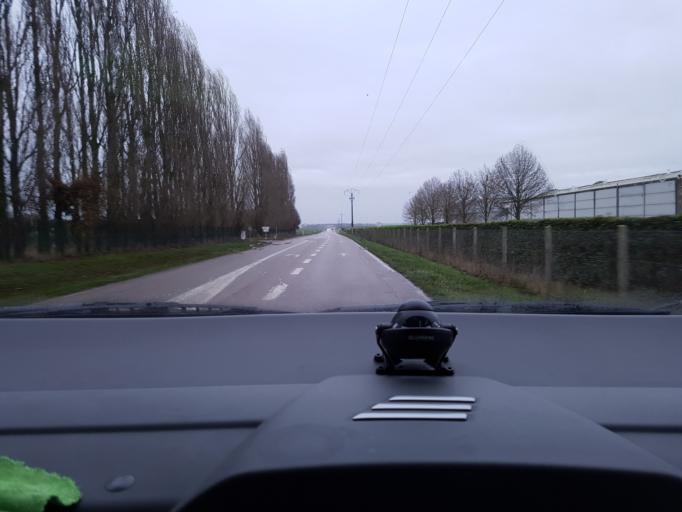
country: FR
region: Haute-Normandie
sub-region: Departement de l'Eure
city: Le Neubourg
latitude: 49.1474
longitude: 0.9384
